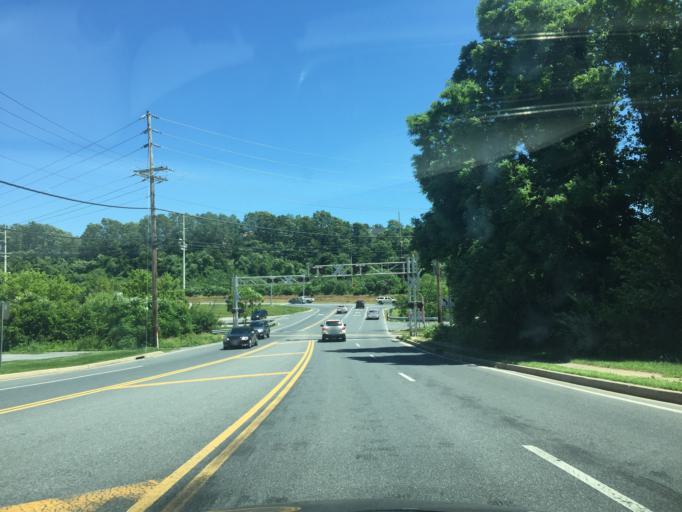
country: US
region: Maryland
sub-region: Carroll County
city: Westminster
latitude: 39.5849
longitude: -76.9808
